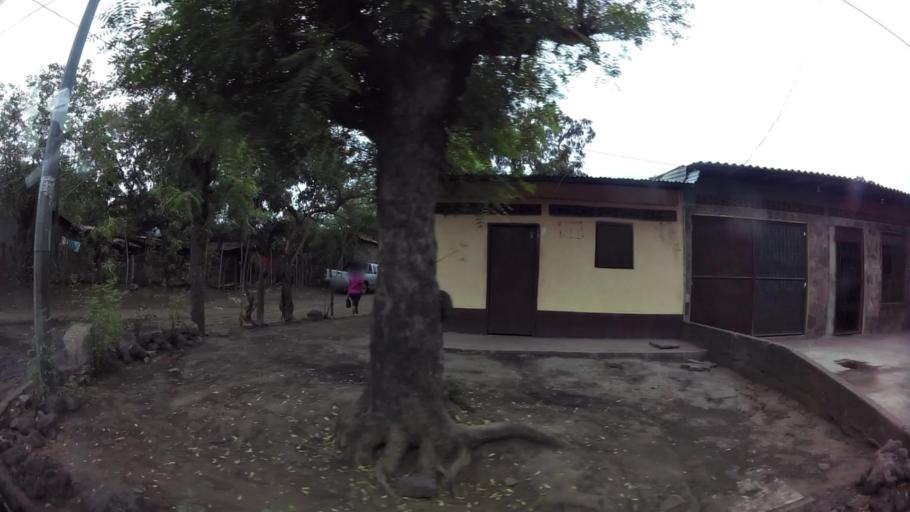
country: NI
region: Leon
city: Leon
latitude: 12.4454
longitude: -86.8698
